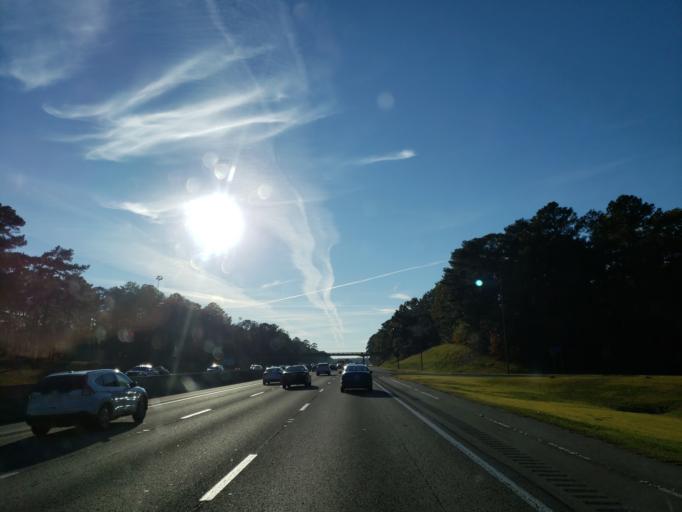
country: US
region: Alabama
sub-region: Tuscaloosa County
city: Coaling
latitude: 33.1894
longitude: -87.3261
